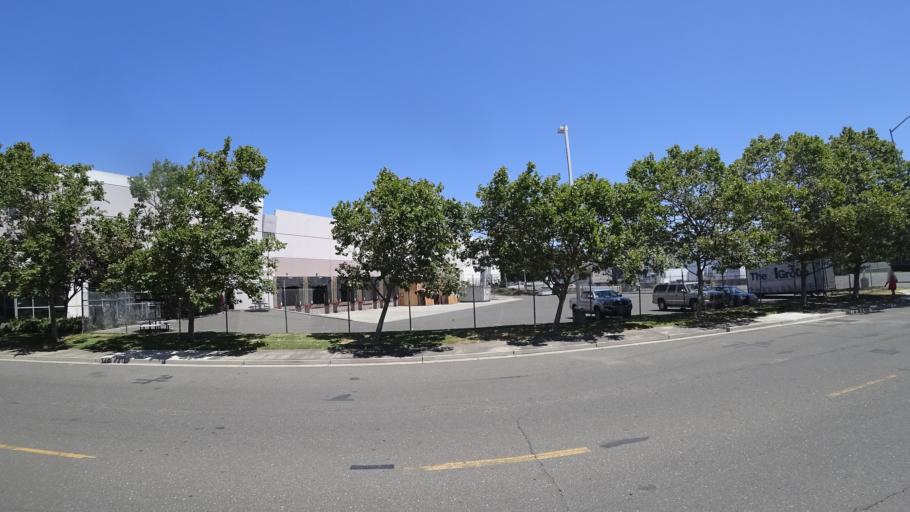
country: US
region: California
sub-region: Alameda County
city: Hayward
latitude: 37.6227
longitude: -122.1160
